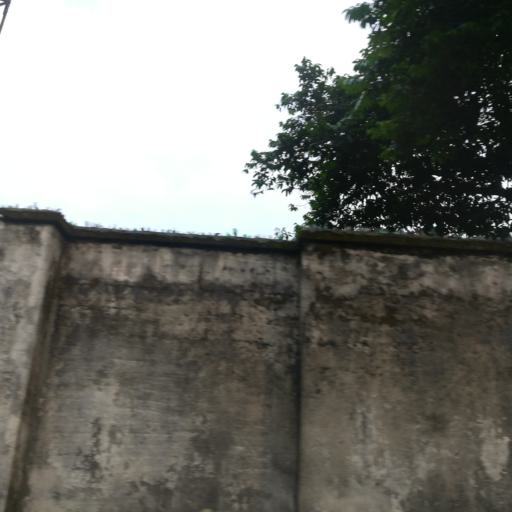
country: NG
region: Rivers
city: Port Harcourt
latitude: 4.8467
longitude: 7.0485
